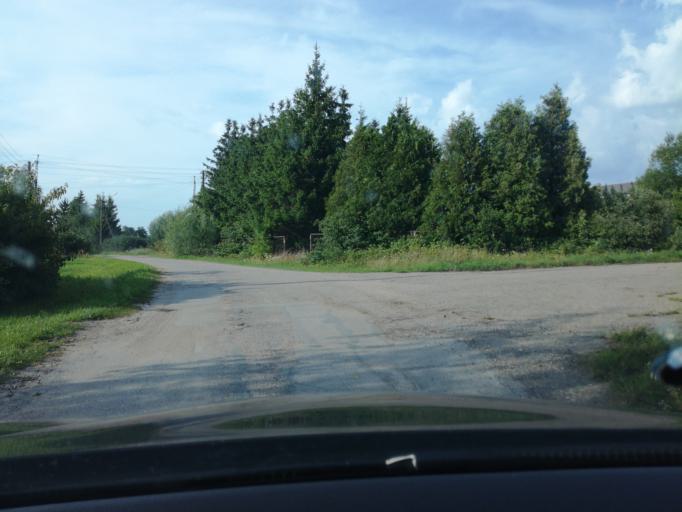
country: LT
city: Simnas
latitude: 54.3813
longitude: 23.6574
